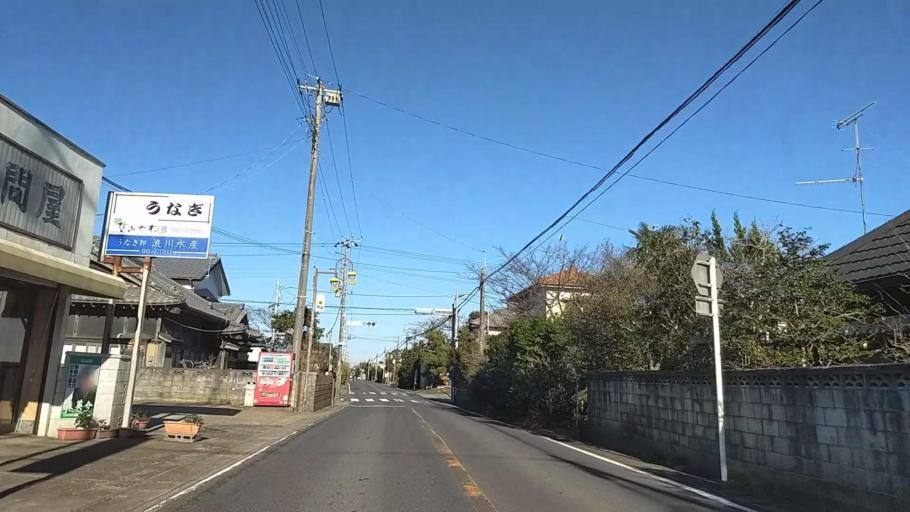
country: JP
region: Chiba
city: Naruto
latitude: 35.5869
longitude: 140.4977
